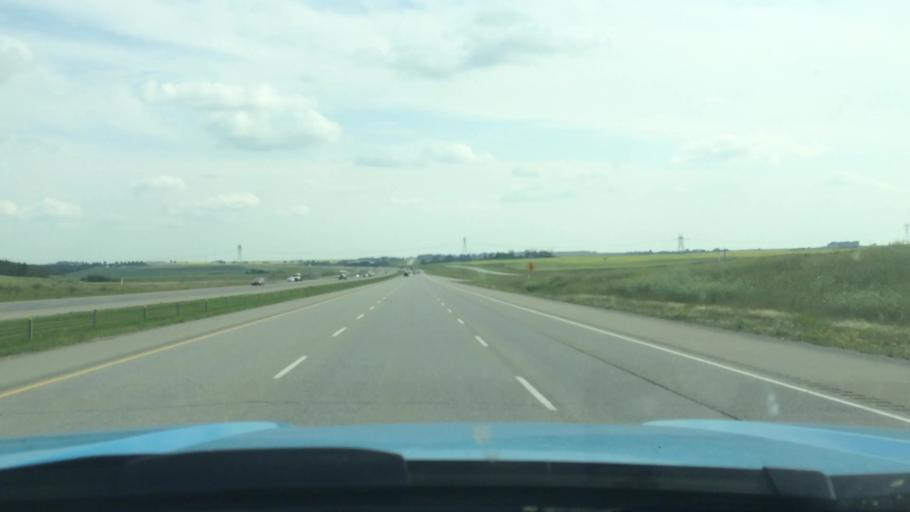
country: CA
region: Alberta
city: Crossfield
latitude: 51.4737
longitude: -114.0252
